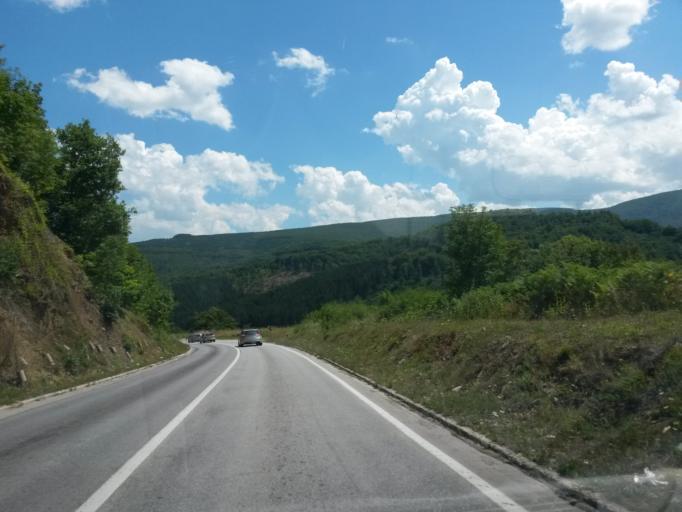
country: BA
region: Federation of Bosnia and Herzegovina
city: Turbe
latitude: 44.2071
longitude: 17.5114
